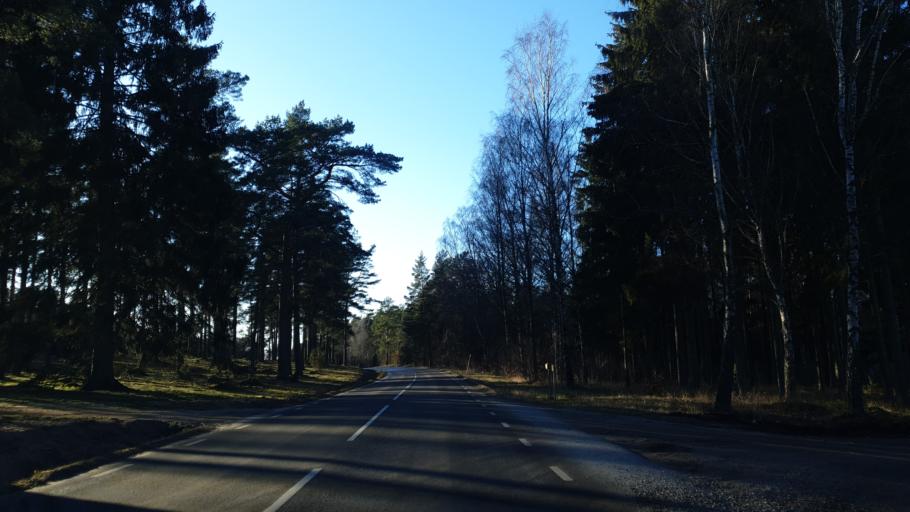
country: SE
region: Blekinge
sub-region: Ronneby Kommun
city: Kallinge
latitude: 56.1956
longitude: 15.3689
